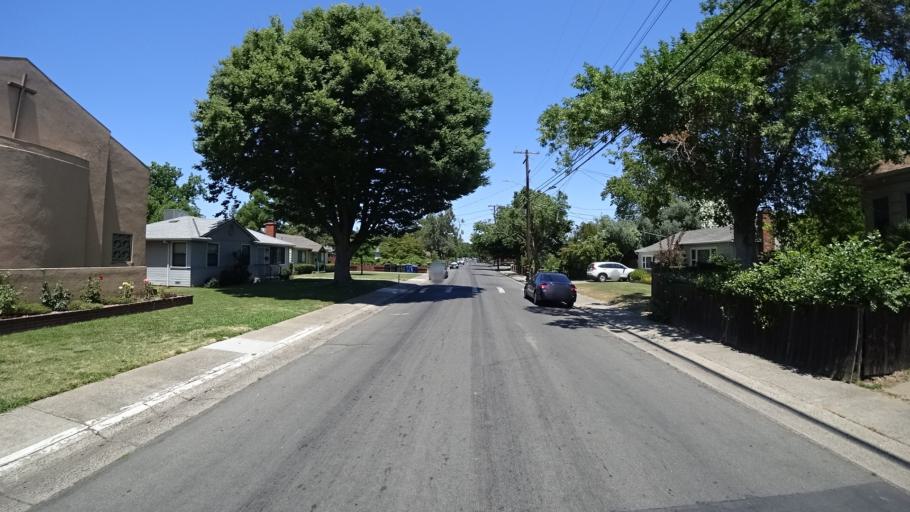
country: US
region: California
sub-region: Sacramento County
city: Parkway
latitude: 38.5351
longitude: -121.4386
